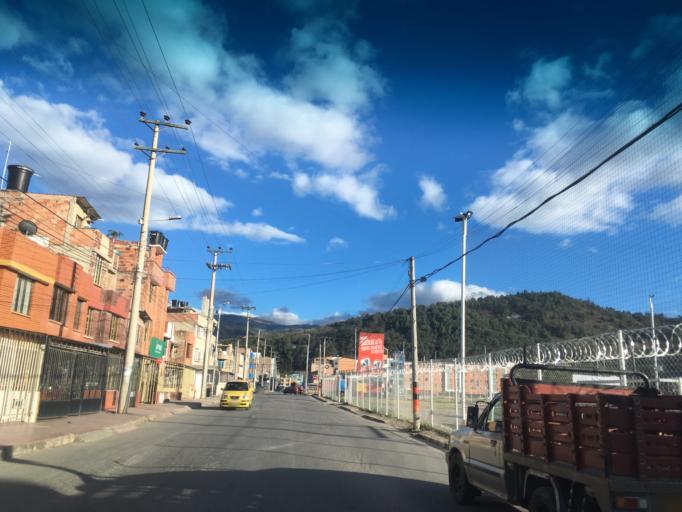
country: CO
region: Boyaca
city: Sogamoso
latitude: 5.7074
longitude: -72.9388
